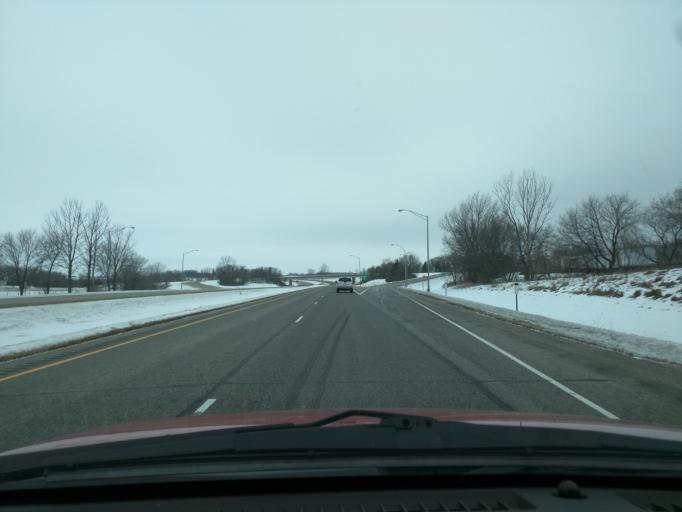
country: US
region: Minnesota
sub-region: Winona County
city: Winona
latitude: 43.9568
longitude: -91.6801
